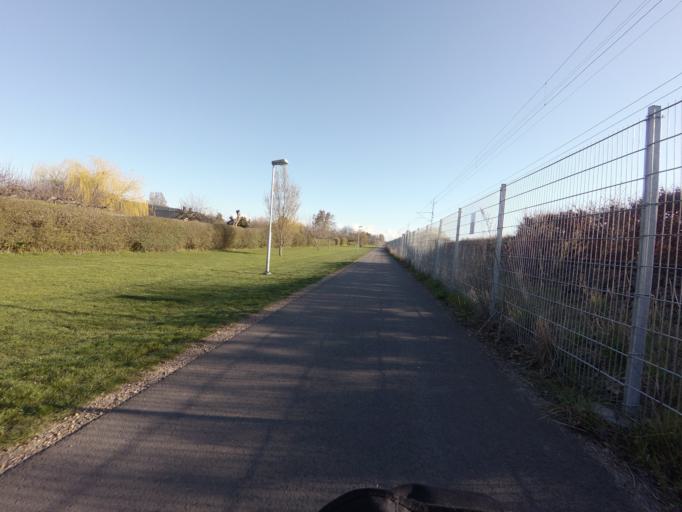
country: SE
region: Skane
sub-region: Lomma Kommun
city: Lomma
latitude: 55.6669
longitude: 13.0745
